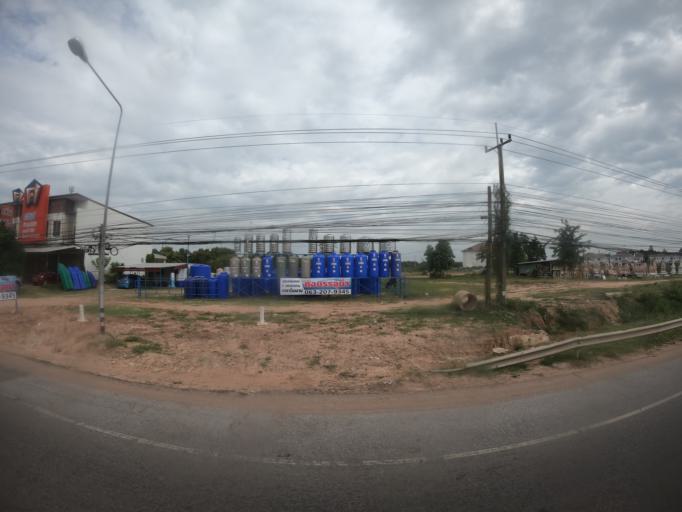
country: TH
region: Maha Sarakham
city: Maha Sarakham
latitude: 16.2136
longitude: 103.2801
